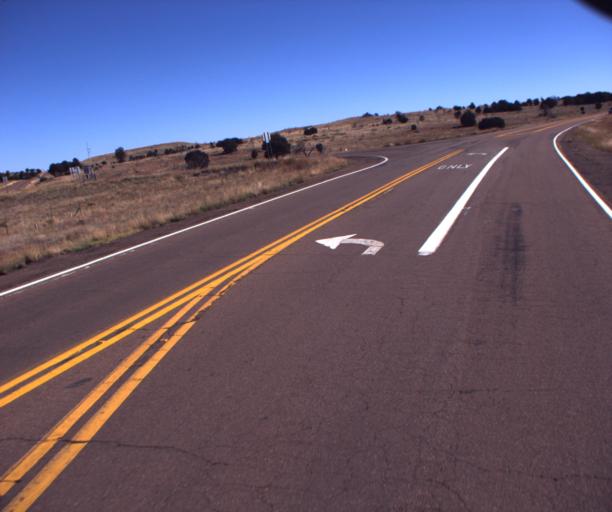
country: US
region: Arizona
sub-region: Navajo County
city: Heber-Overgaard
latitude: 34.4637
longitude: -110.4773
